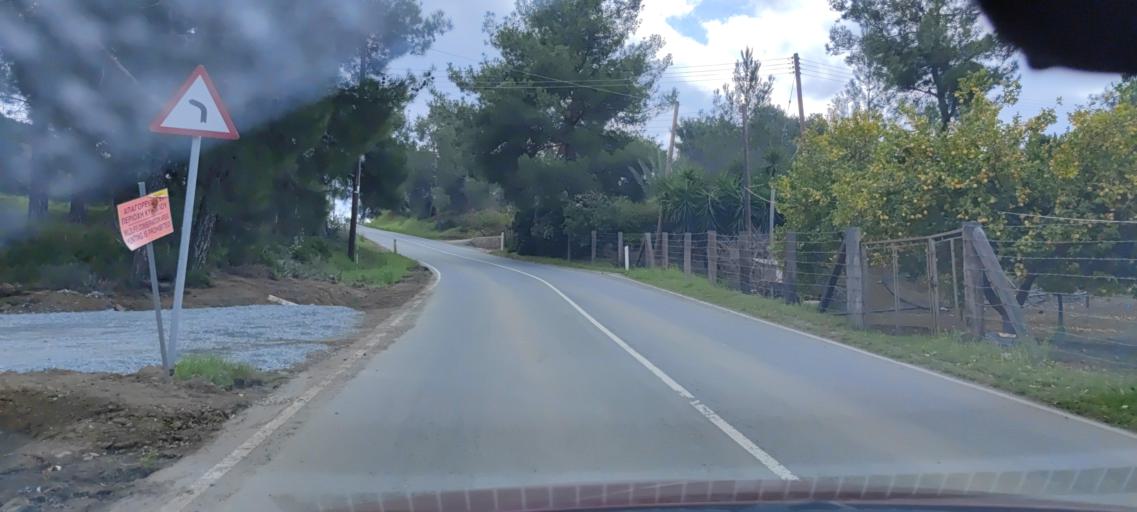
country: CY
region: Lefkosia
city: Lythrodontas
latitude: 34.9702
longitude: 33.2916
